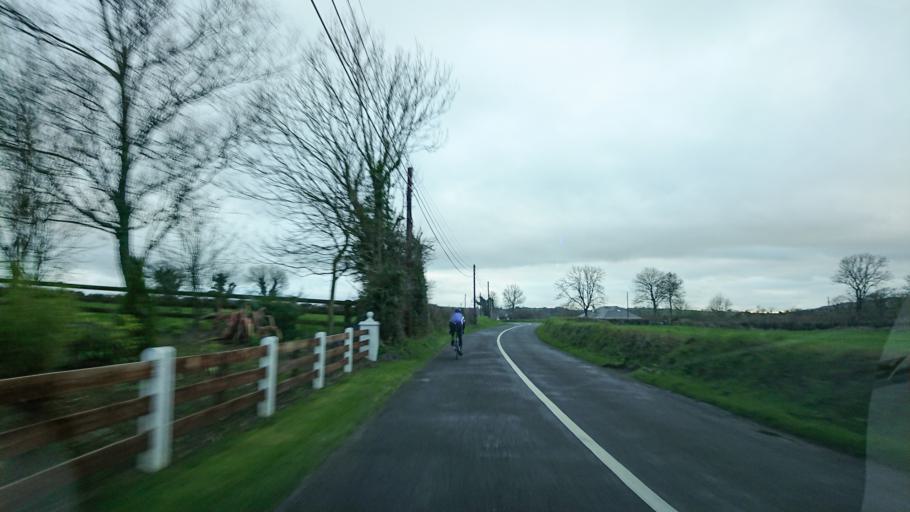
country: IE
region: Munster
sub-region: Waterford
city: Portlaw
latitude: 52.1848
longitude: -7.4085
